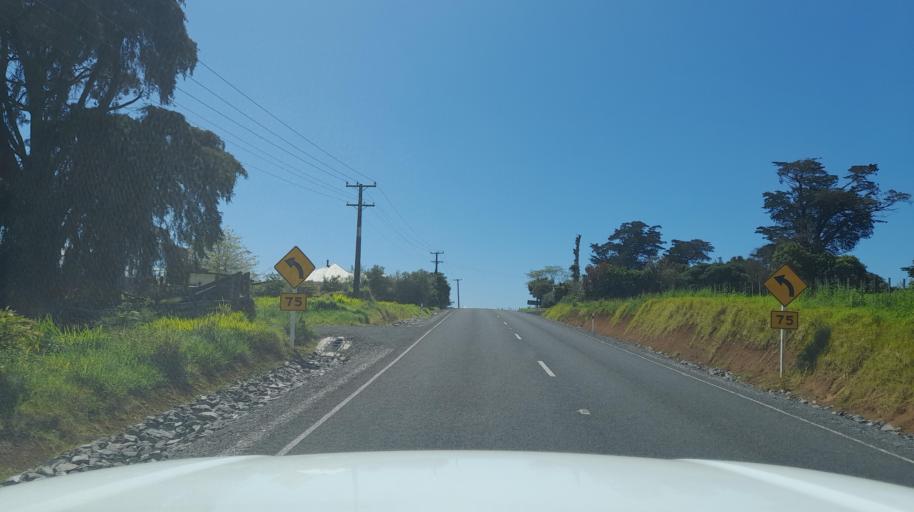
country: NZ
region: Northland
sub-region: Far North District
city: Taipa
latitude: -35.0559
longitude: 173.5014
